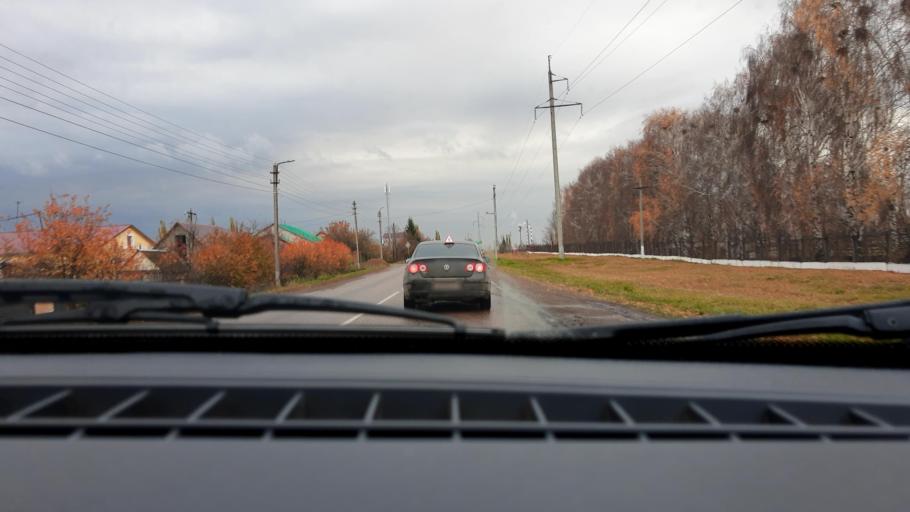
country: RU
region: Bashkortostan
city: Ufa
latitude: 54.8358
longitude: 55.9965
